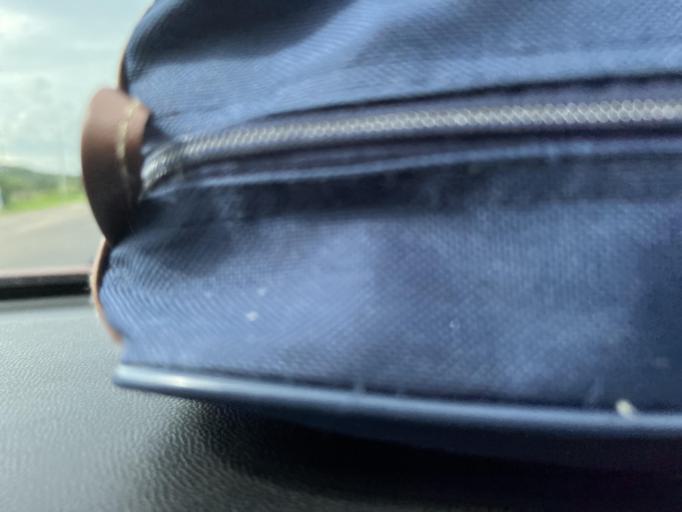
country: SV
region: La Union
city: San Alejo
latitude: 13.3881
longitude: -87.9034
